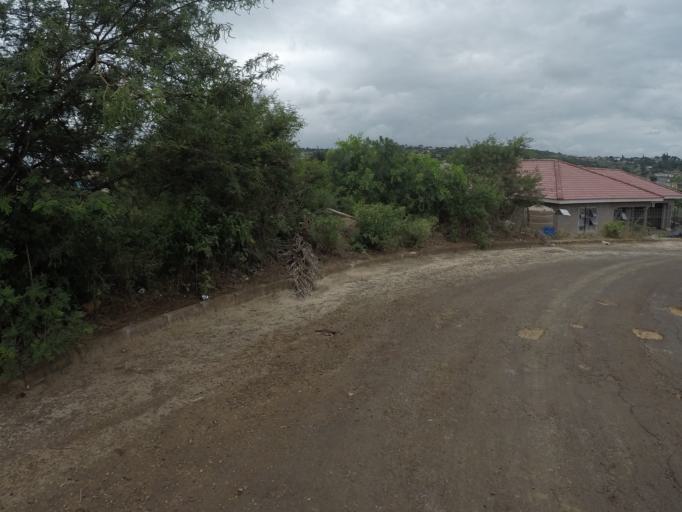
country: ZA
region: KwaZulu-Natal
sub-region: uThungulu District Municipality
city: Empangeni
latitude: -28.7802
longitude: 31.8561
